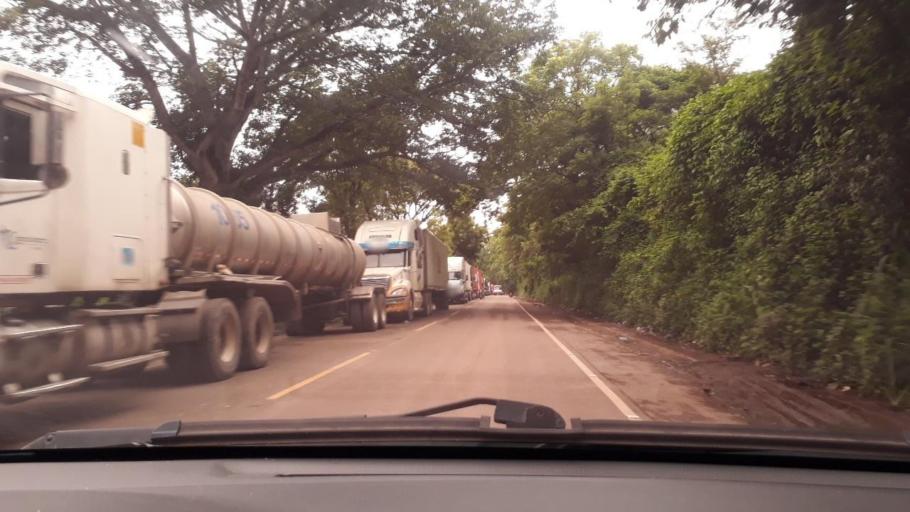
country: SV
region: Santa Ana
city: Metapan
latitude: 14.4229
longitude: -89.4472
